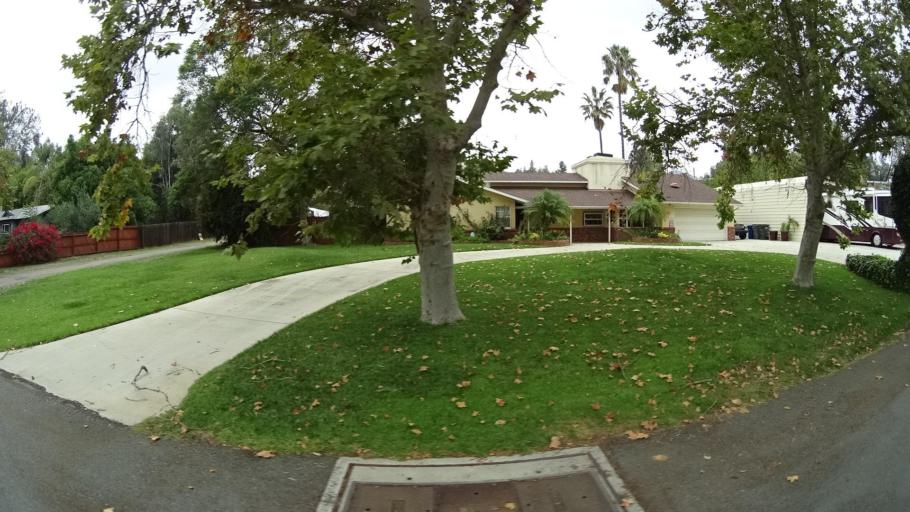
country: US
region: California
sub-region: San Diego County
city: Spring Valley
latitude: 32.7468
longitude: -116.9934
